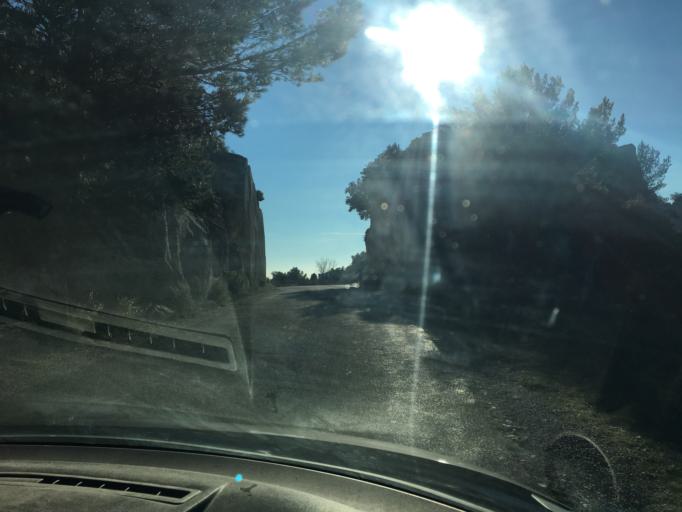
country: FR
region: Provence-Alpes-Cote d'Azur
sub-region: Departement des Bouches-du-Rhone
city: Maussane-les-Alpilles
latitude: 43.7525
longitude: 4.7914
